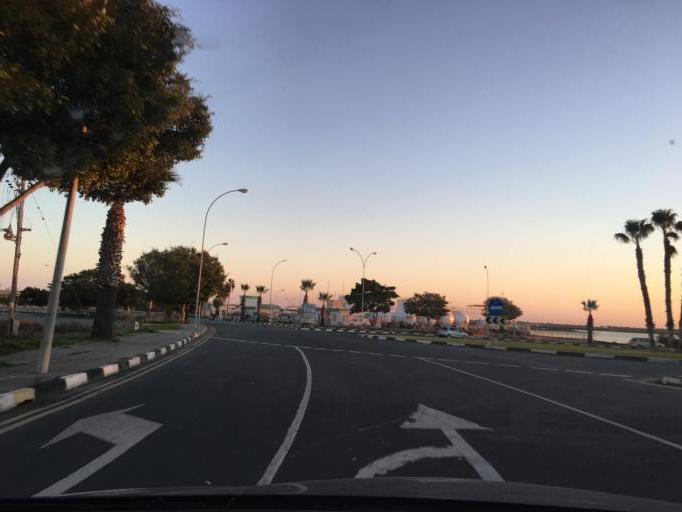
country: CY
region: Larnaka
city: Meneou
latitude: 34.8841
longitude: 33.6225
